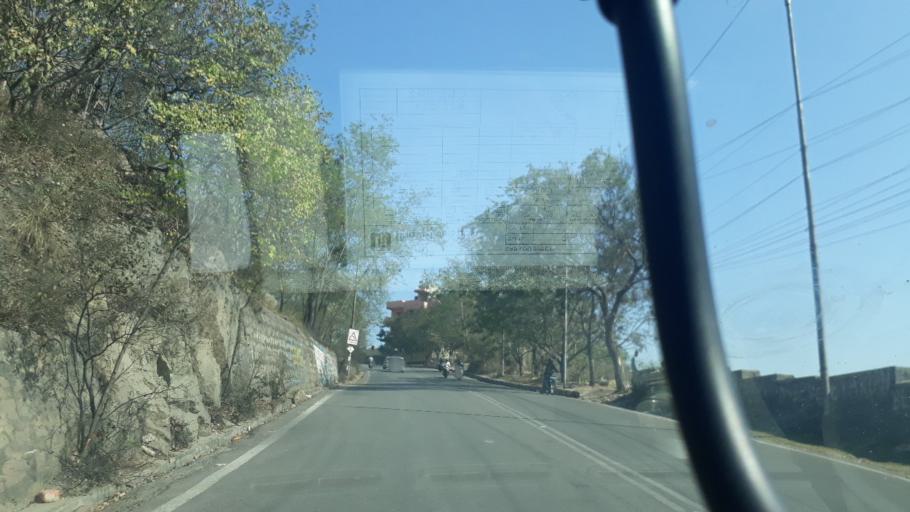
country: IN
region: Telangana
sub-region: Hyderabad
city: Hyderabad
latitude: 17.4178
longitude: 78.3966
